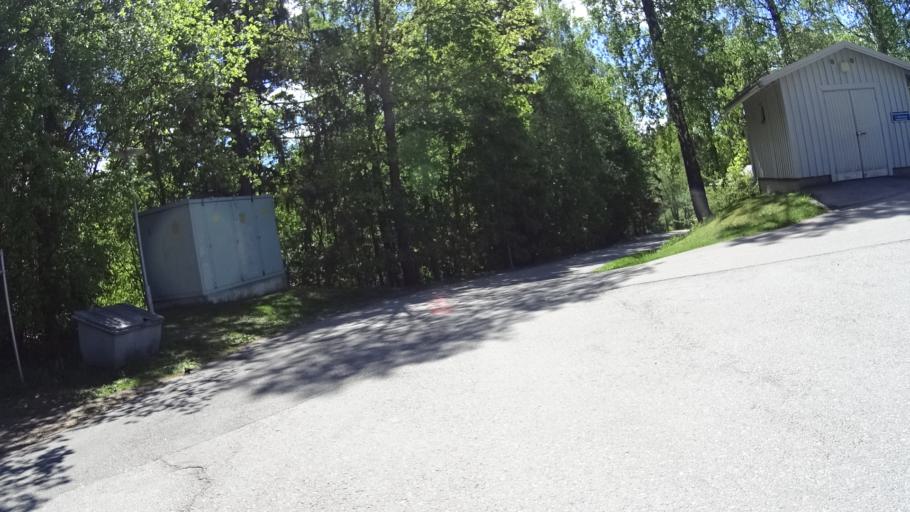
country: FI
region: Uusimaa
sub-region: Helsinki
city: Kauniainen
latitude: 60.2214
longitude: 24.6946
